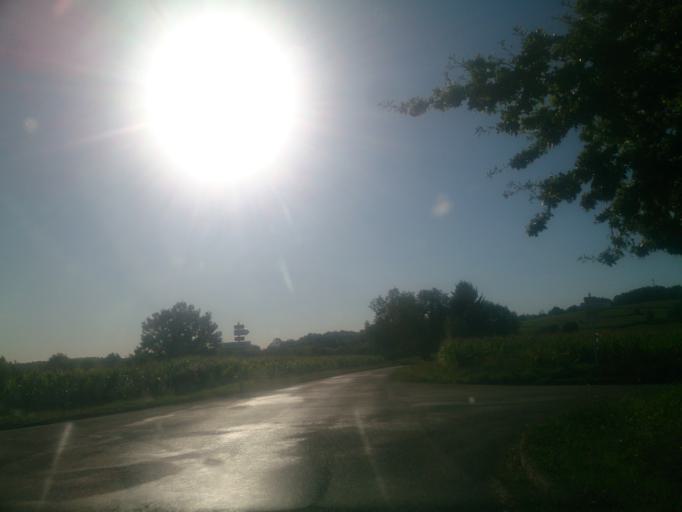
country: FR
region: Midi-Pyrenees
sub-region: Departement des Hautes-Pyrenees
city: Horgues
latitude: 43.1369
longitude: 0.0791
